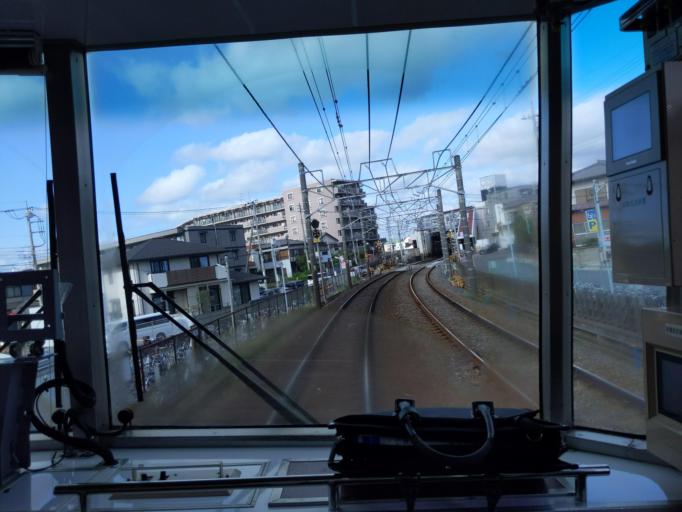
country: JP
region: Chiba
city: Funabashi
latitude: 35.7366
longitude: 140.0250
